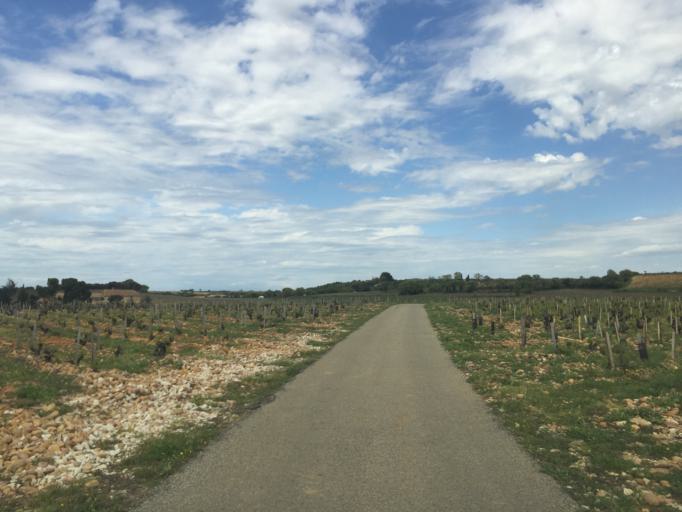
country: FR
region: Provence-Alpes-Cote d'Azur
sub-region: Departement du Vaucluse
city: Chateauneuf-du-Pape
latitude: 44.0543
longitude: 4.8547
